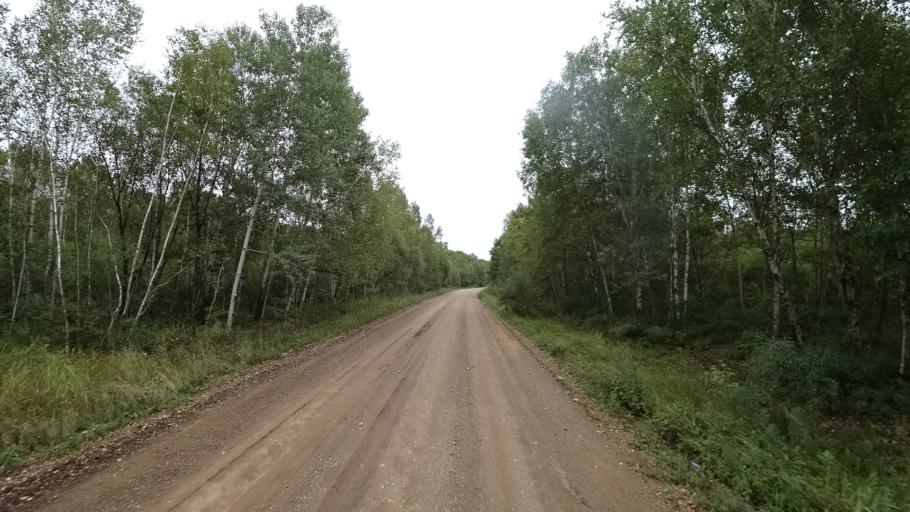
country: RU
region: Primorskiy
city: Ivanovka
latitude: 44.0278
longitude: 132.5146
